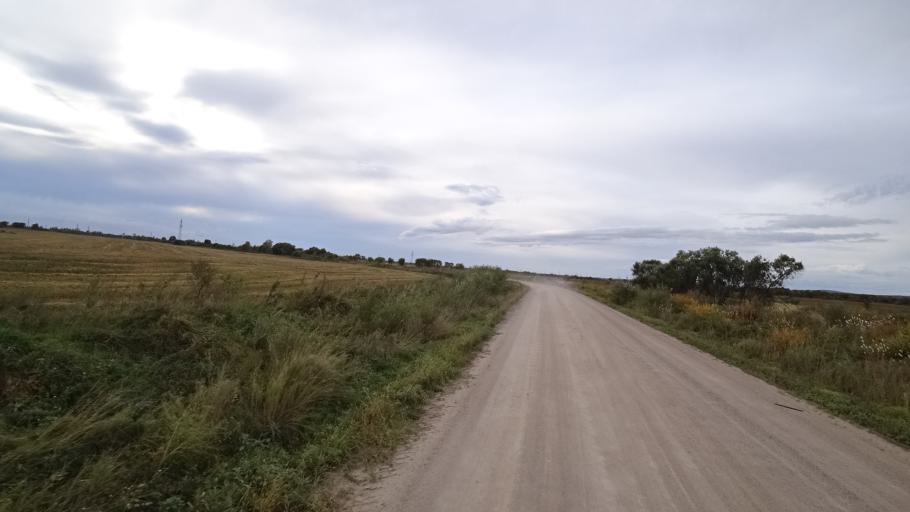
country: RU
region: Amur
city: Arkhara
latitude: 49.3753
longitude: 130.1566
